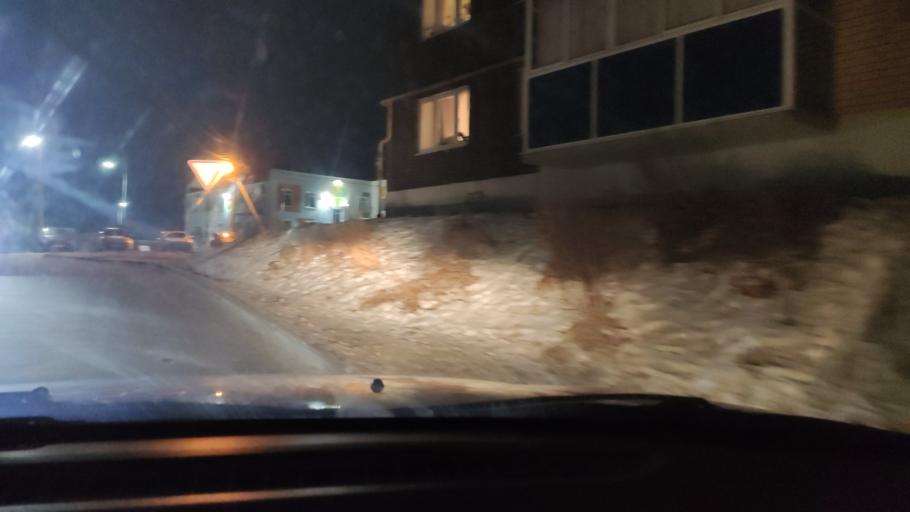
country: RU
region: Perm
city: Ferma
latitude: 57.8938
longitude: 56.3278
